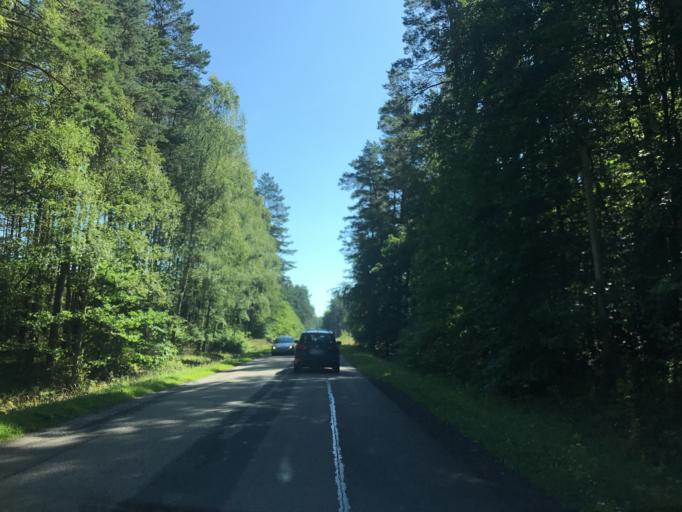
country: PL
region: Pomeranian Voivodeship
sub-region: Powiat bytowski
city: Czarna Dabrowka
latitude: 54.3391
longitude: 17.6434
